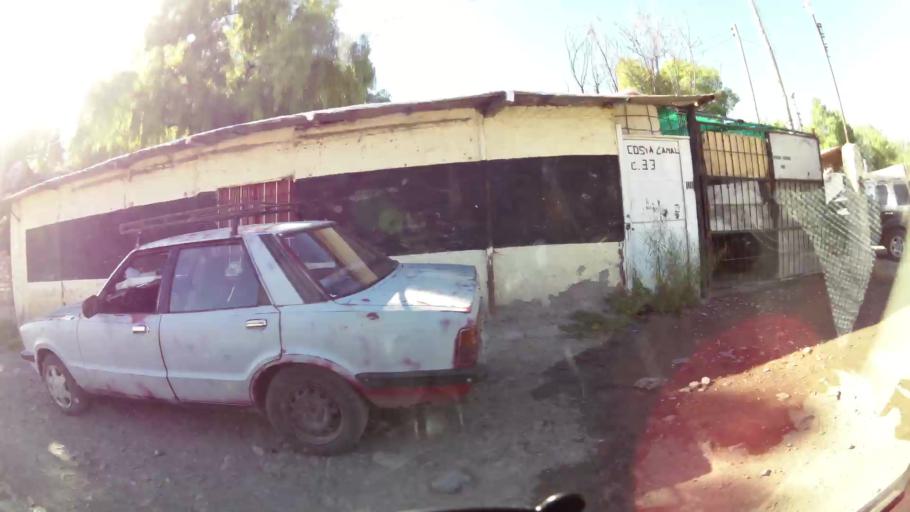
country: AR
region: Mendoza
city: Las Heras
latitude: -32.8701
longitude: -68.8624
